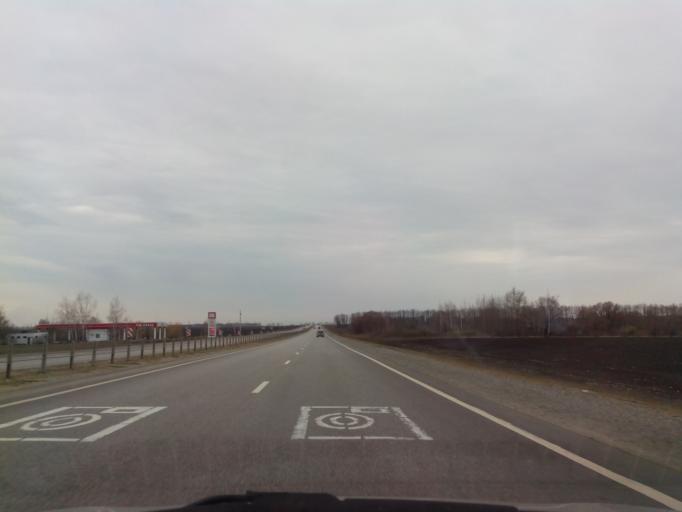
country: RU
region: Tambov
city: Zavoronezhskoye
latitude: 52.9001
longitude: 40.6640
